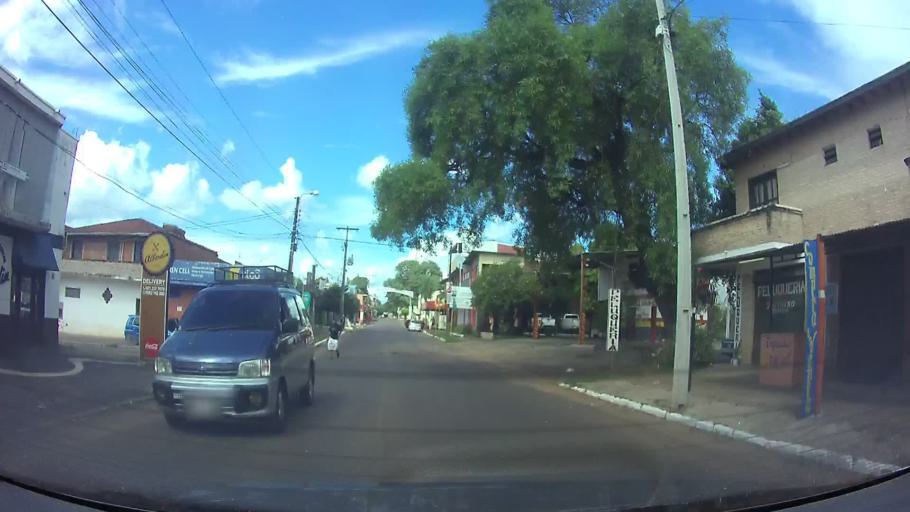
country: PY
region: Central
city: Villa Elisa
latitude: -25.3412
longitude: -57.5744
